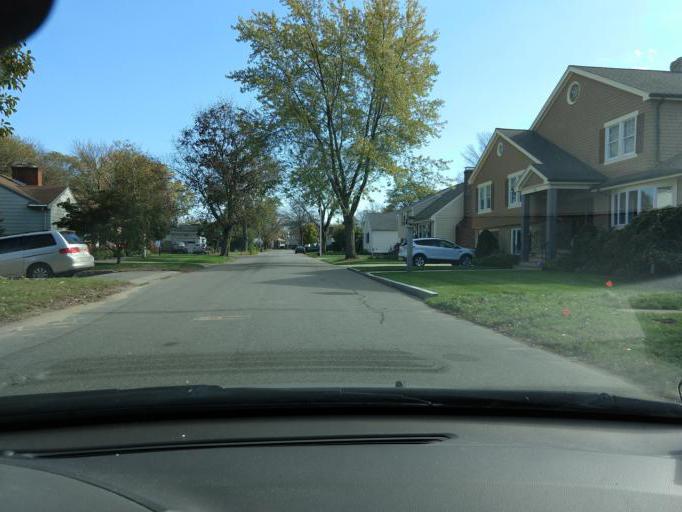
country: US
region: Massachusetts
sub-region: Middlesex County
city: Belmont
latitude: 42.3975
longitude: -71.1673
